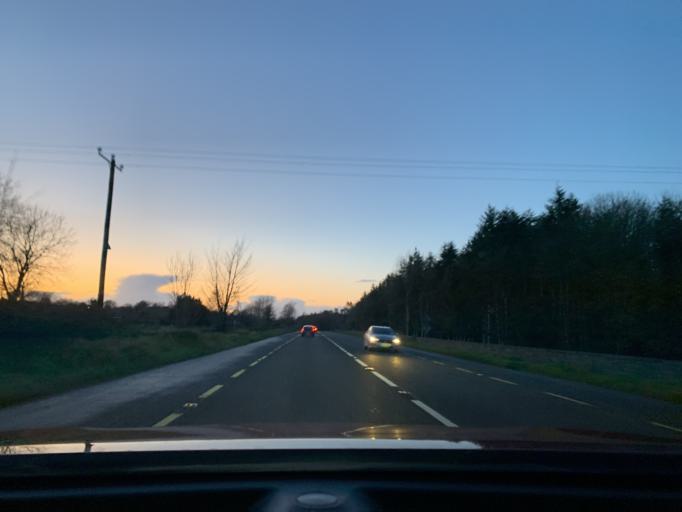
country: IE
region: Connaught
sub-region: Roscommon
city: Boyle
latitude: 53.9694
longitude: -8.2351
